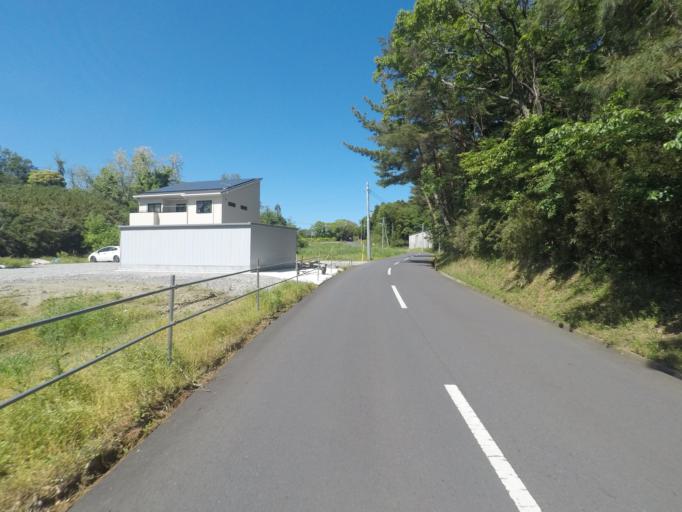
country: JP
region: Ibaraki
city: Itako
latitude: 36.0027
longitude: 140.4761
